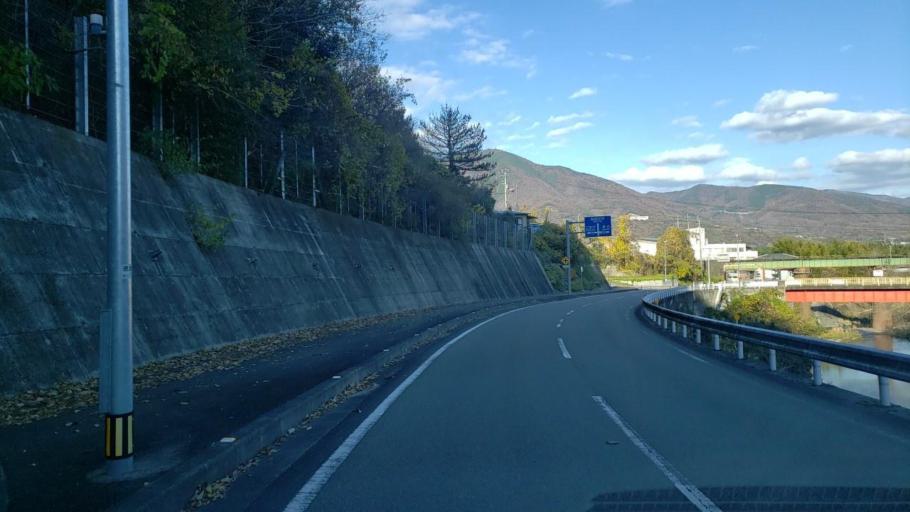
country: JP
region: Tokushima
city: Wakimachi
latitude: 34.0399
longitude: 134.0272
